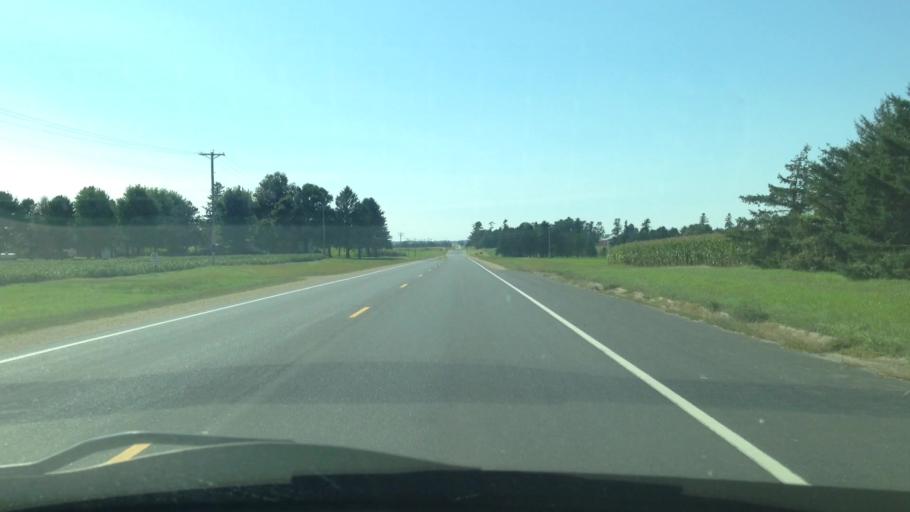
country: US
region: Minnesota
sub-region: Winona County
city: Lewiston
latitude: 43.9699
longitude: -91.8437
